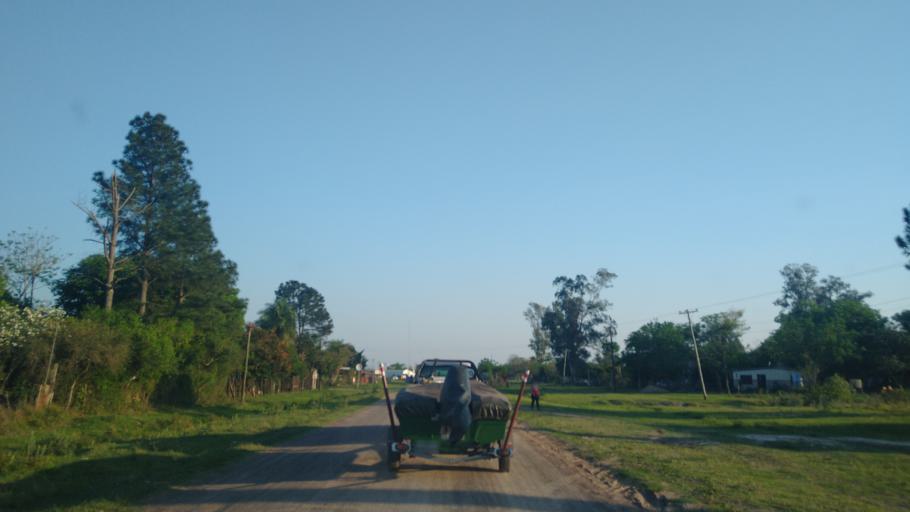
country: PY
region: Neembucu
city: Cerrito
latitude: -27.3747
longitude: -57.6549
